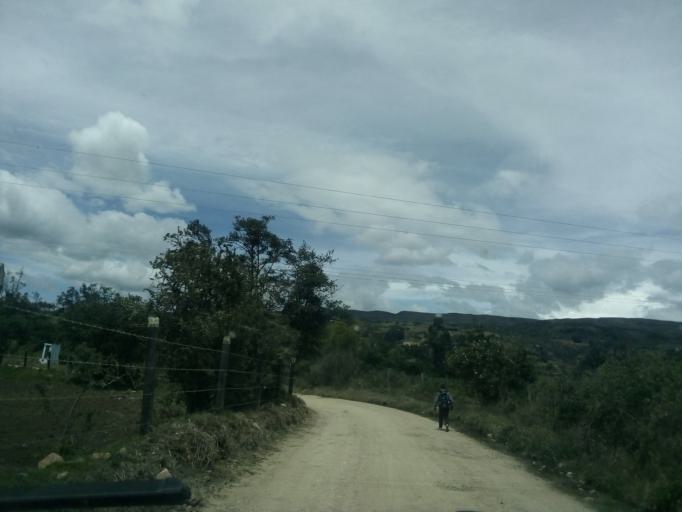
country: CO
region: Boyaca
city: Toca
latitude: 5.6186
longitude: -73.1420
